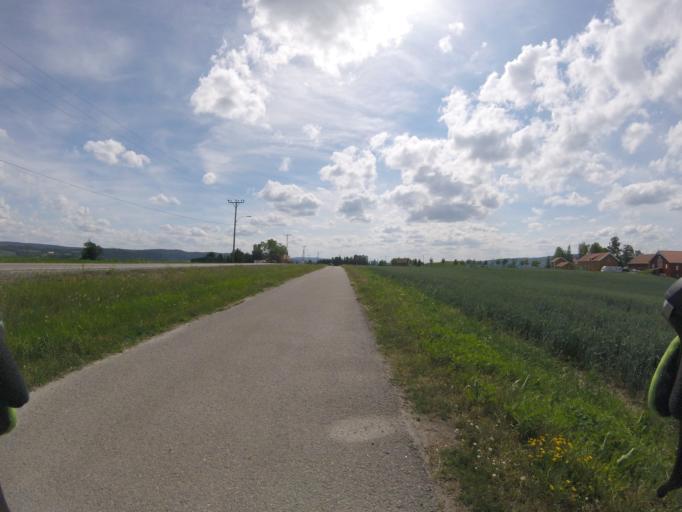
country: NO
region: Akershus
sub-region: Skedsmo
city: Lillestrom
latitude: 59.9808
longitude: 11.0533
